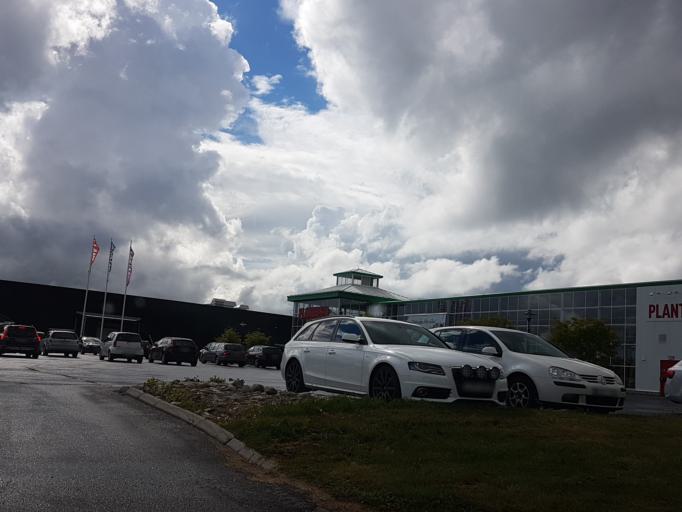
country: SE
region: Vaesterbotten
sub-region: Umea Kommun
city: Ersmark
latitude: 63.8556
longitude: 20.3019
